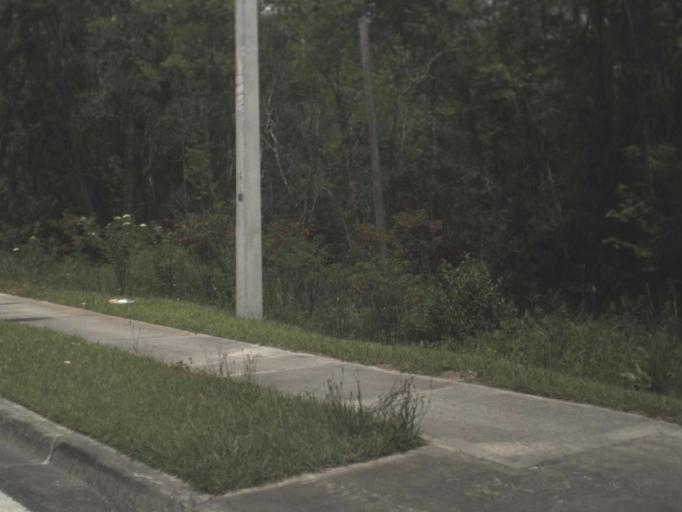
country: US
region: Florida
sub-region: Columbia County
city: Five Points
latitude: 30.2068
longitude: -82.6374
